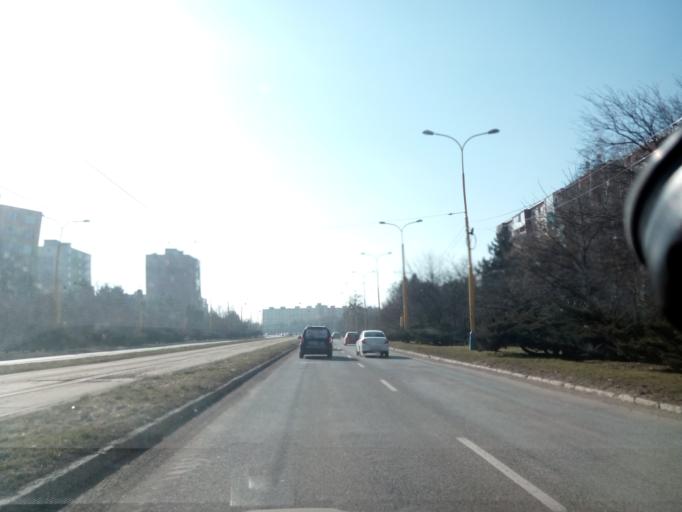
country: SK
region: Kosicky
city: Kosice
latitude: 48.7129
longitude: 21.2356
